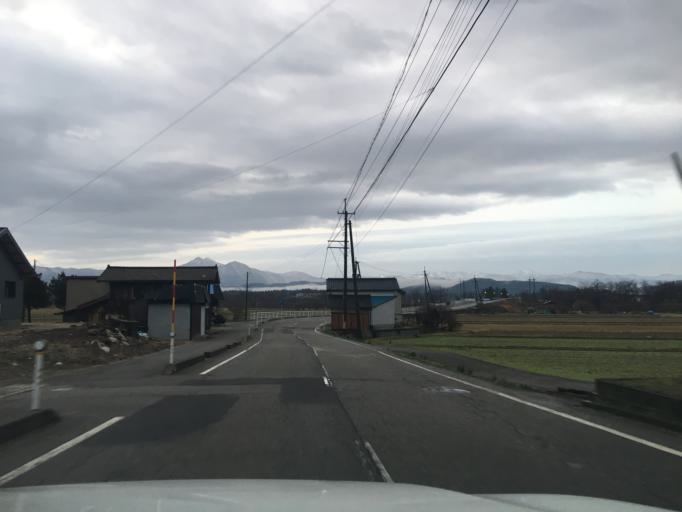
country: JP
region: Niigata
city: Murakami
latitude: 38.2745
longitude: 139.5261
